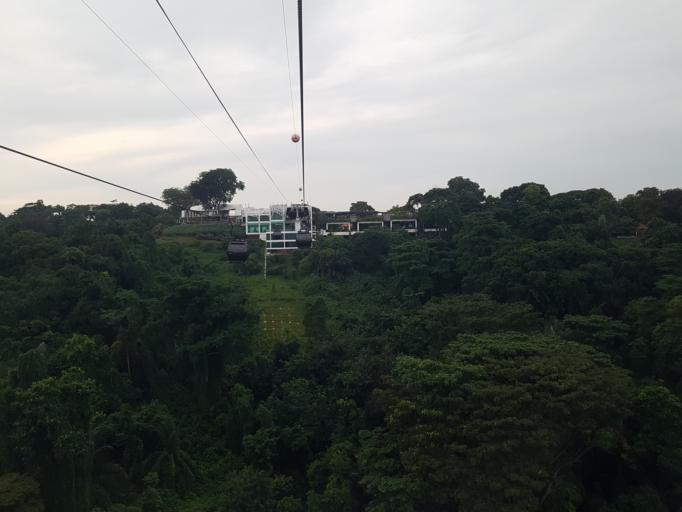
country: SG
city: Singapore
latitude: 1.2688
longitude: 103.8192
